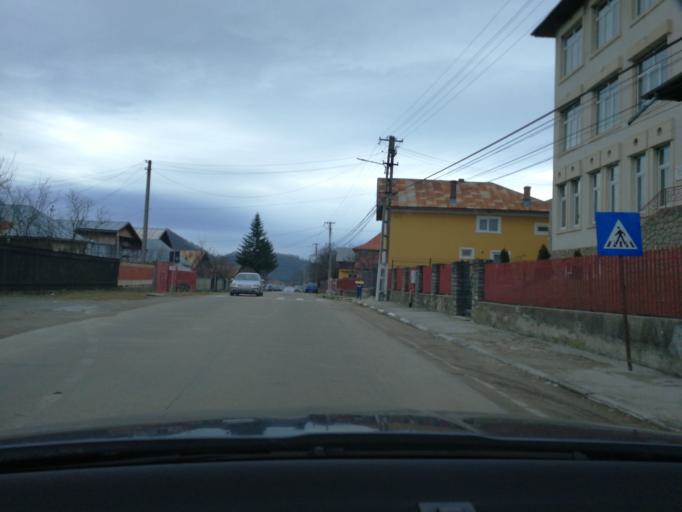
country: RO
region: Dambovita
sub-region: Comuna Bezdead
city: Bezdead
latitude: 45.1579
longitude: 25.5291
